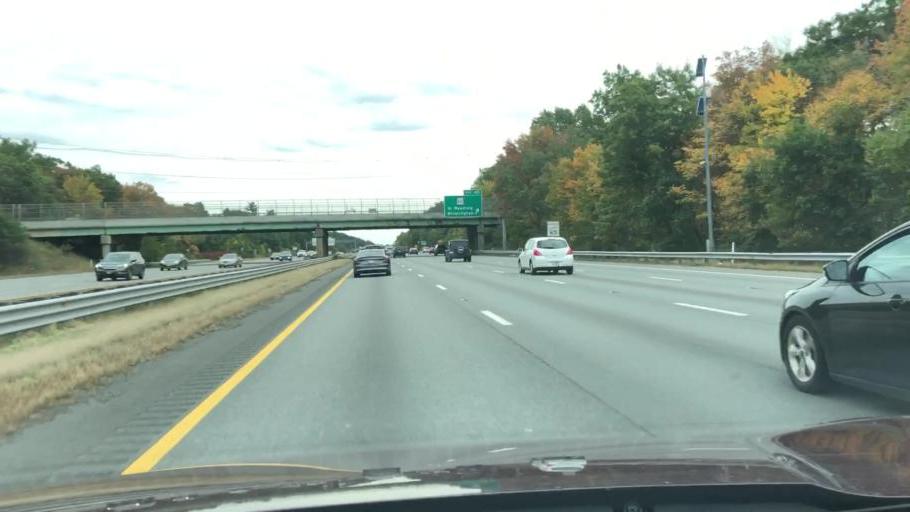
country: US
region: Massachusetts
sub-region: Middlesex County
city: Wilmington
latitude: 42.5781
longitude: -71.1529
